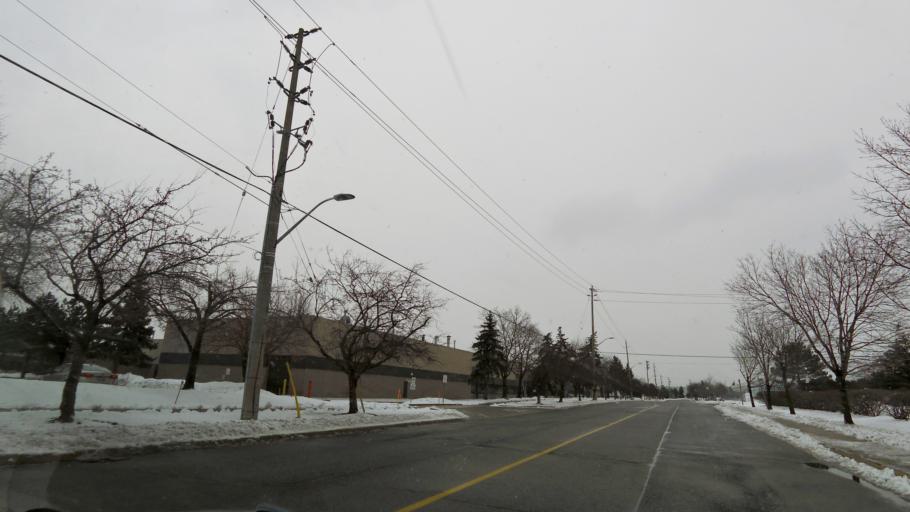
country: CA
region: Ontario
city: Mississauga
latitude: 43.6619
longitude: -79.6664
